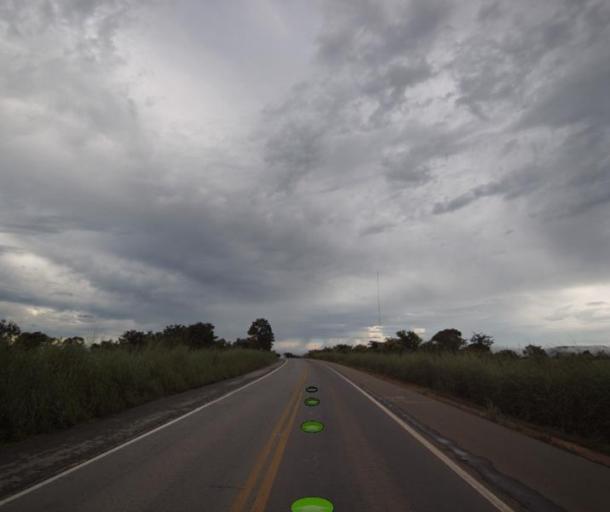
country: BR
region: Goias
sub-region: Porangatu
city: Porangatu
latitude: -13.4861
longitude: -49.1364
